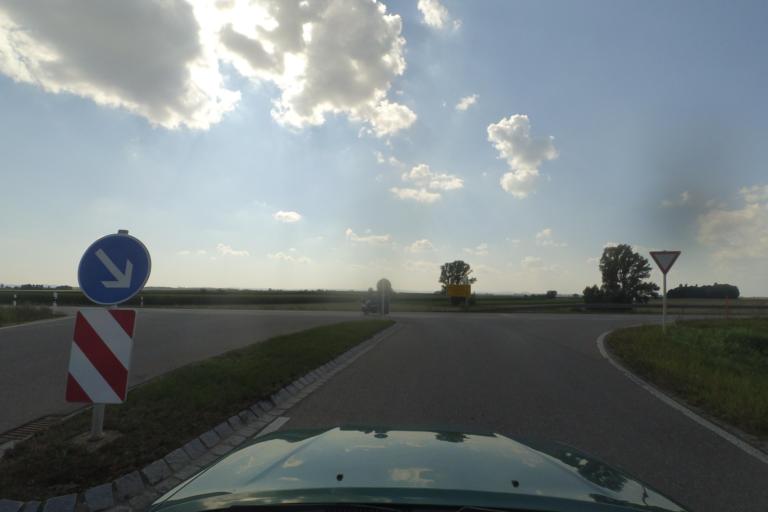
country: DE
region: Bavaria
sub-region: Swabia
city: Munningen
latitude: 48.9105
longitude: 10.6048
